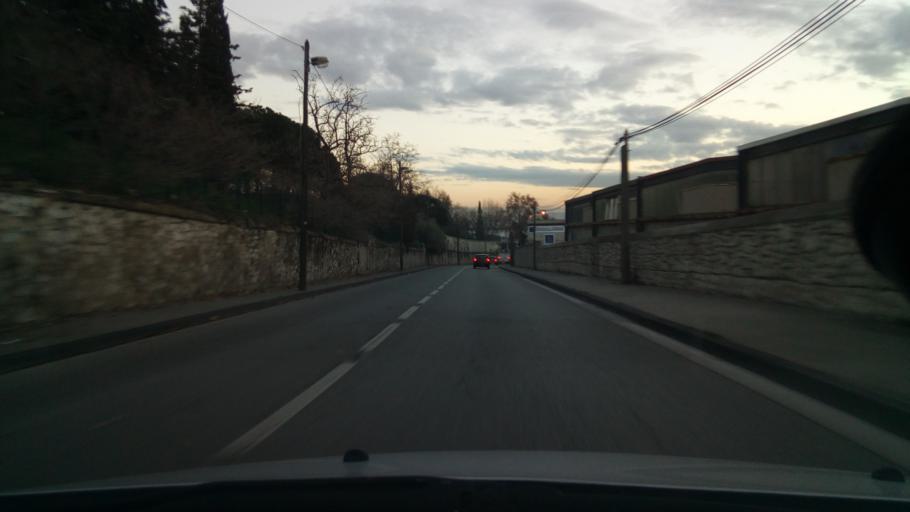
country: FR
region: Provence-Alpes-Cote d'Azur
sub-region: Departement des Bouches-du-Rhone
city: Marseille 14
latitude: 43.3353
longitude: 5.3674
